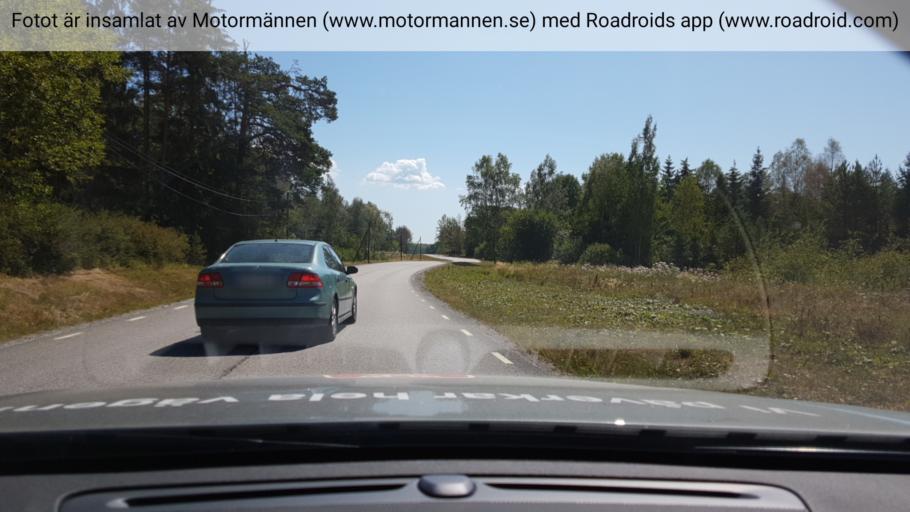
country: SE
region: Stockholm
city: Stenhamra
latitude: 59.3729
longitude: 17.7050
